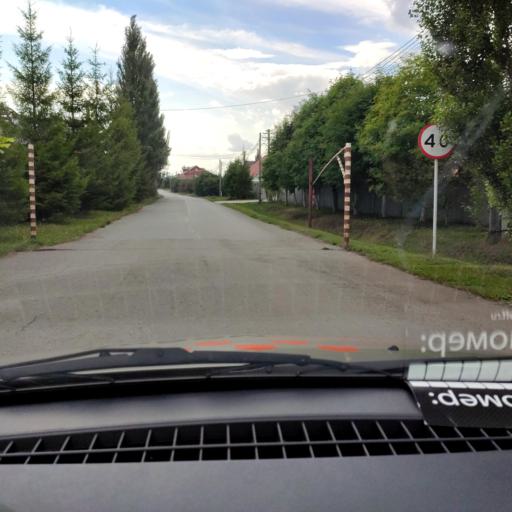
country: RU
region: Bashkortostan
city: Ufa
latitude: 54.6151
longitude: 55.9205
